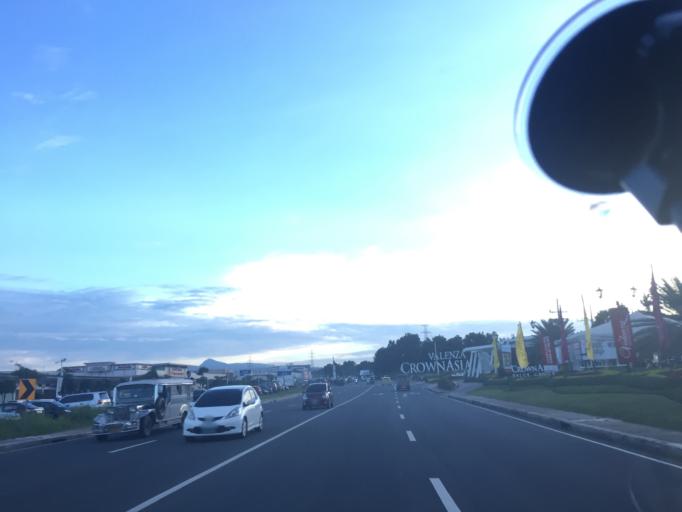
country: PH
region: Calabarzon
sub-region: Province of Cavite
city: Puting Kahoy
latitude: 14.2392
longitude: 121.0562
